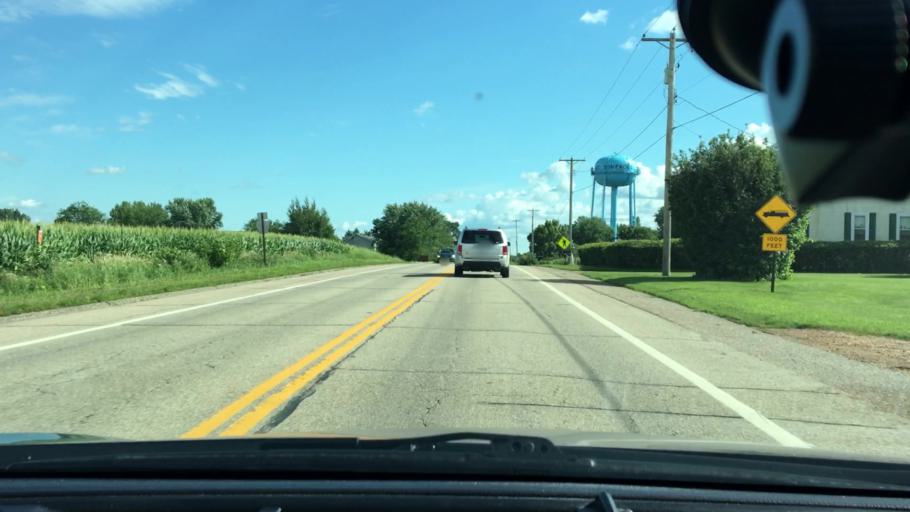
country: US
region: Minnesota
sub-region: Hennepin County
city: Saint Bonifacius
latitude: 44.9148
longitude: -93.7473
